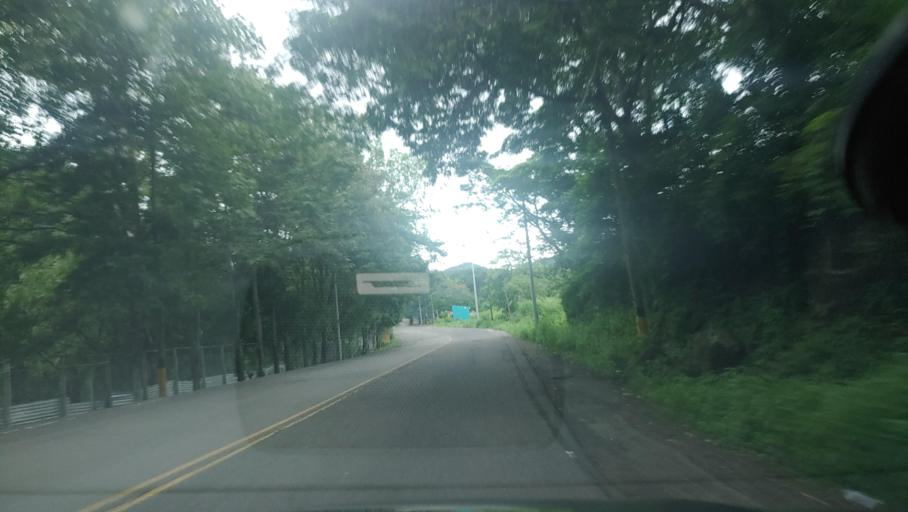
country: HN
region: Choluteca
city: Corpus
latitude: 13.3711
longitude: -87.0371
